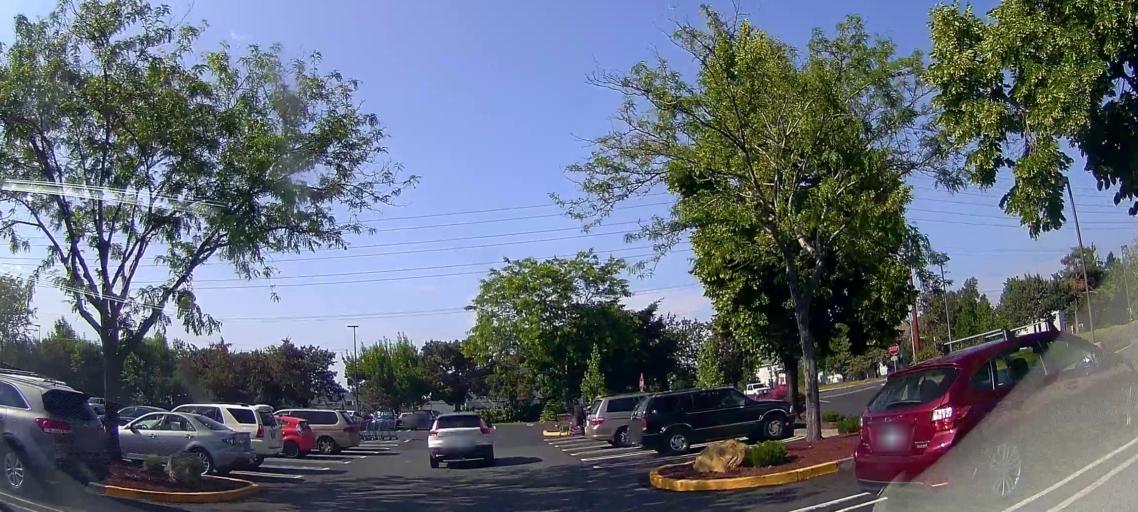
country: US
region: Oregon
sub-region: Deschutes County
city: Bend
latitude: 44.0579
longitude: -121.2666
